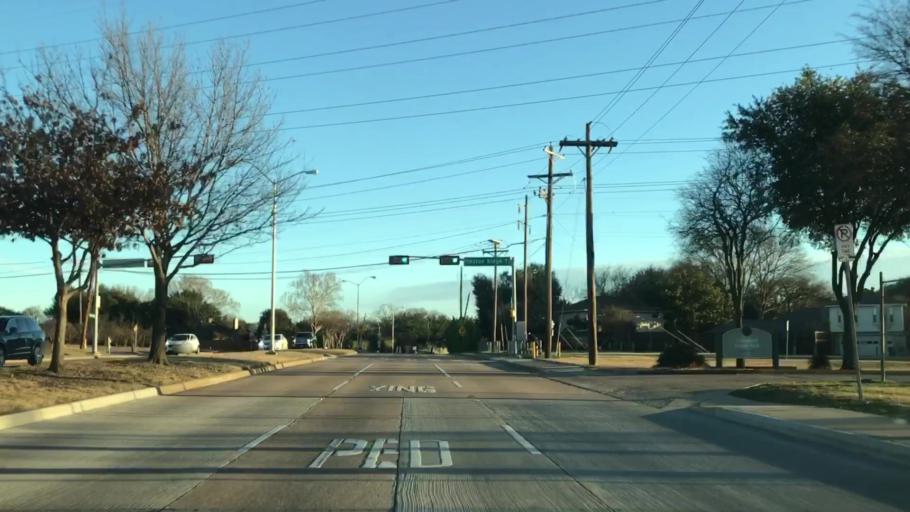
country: US
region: Texas
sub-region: Dallas County
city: Addison
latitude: 32.9769
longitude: -96.7852
